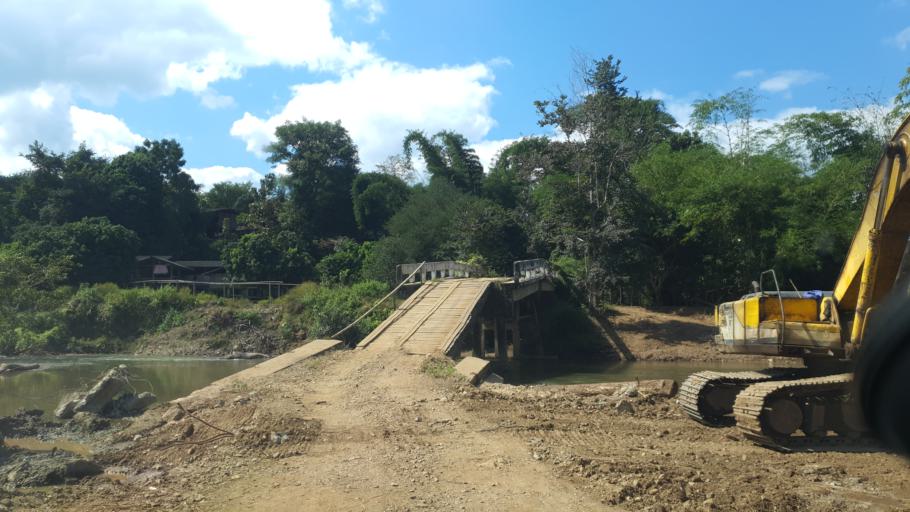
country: TH
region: Mae Hong Son
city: Mae Hi
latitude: 19.2958
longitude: 98.7084
